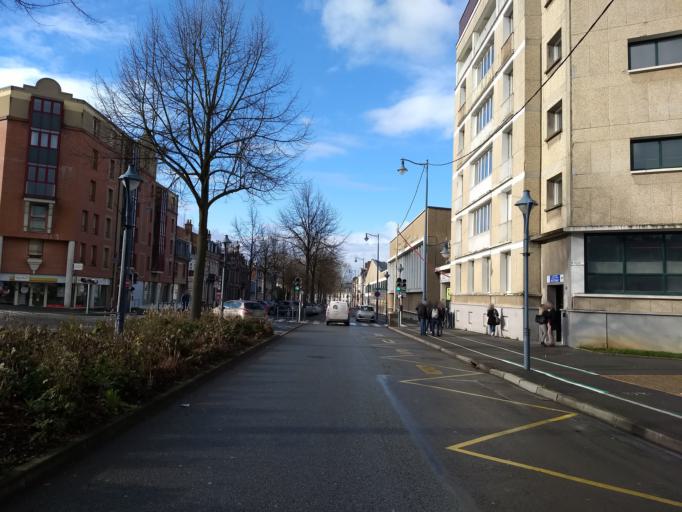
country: FR
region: Nord-Pas-de-Calais
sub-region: Departement du Pas-de-Calais
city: Arras
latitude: 50.2875
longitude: 2.7748
